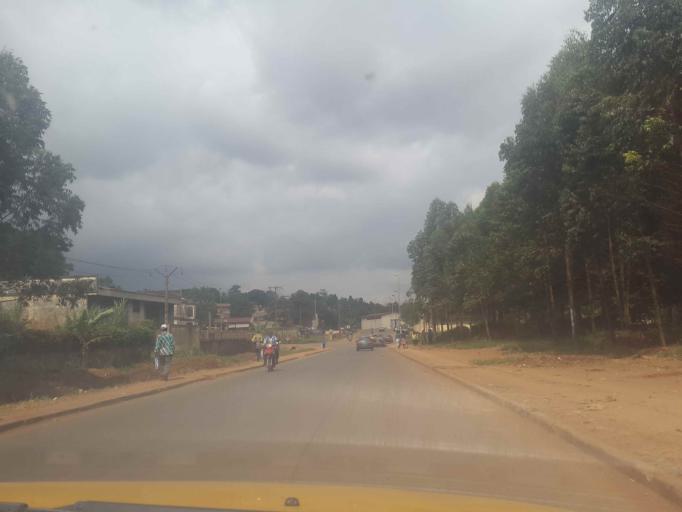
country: CM
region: Centre
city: Yaounde
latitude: 3.8716
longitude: 11.4832
